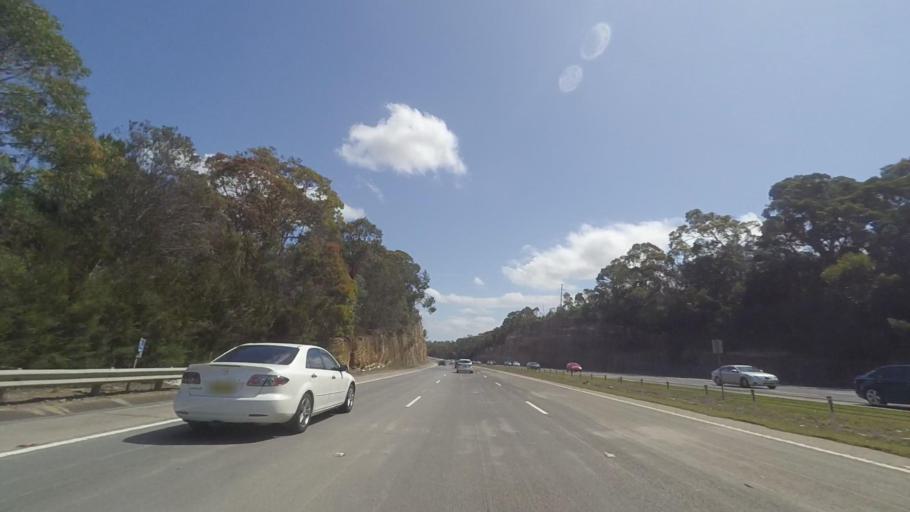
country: AU
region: New South Wales
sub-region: Hornsby Shire
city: Mount Colah
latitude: -33.6646
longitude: 151.1244
